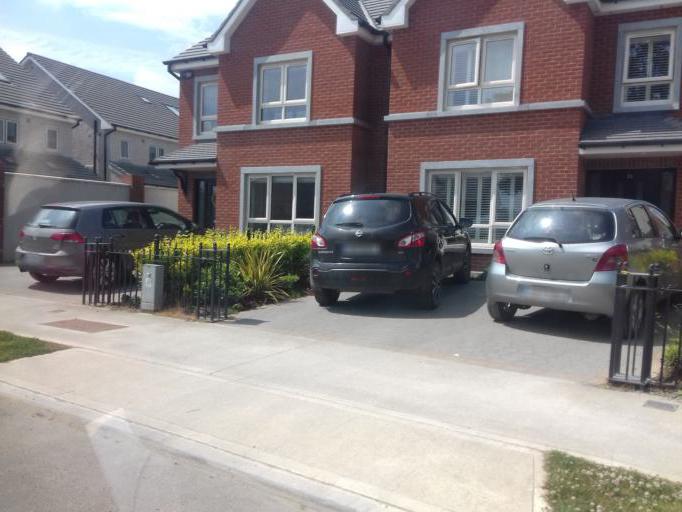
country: IE
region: Leinster
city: Donabate
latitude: 53.4897
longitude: -6.1615
